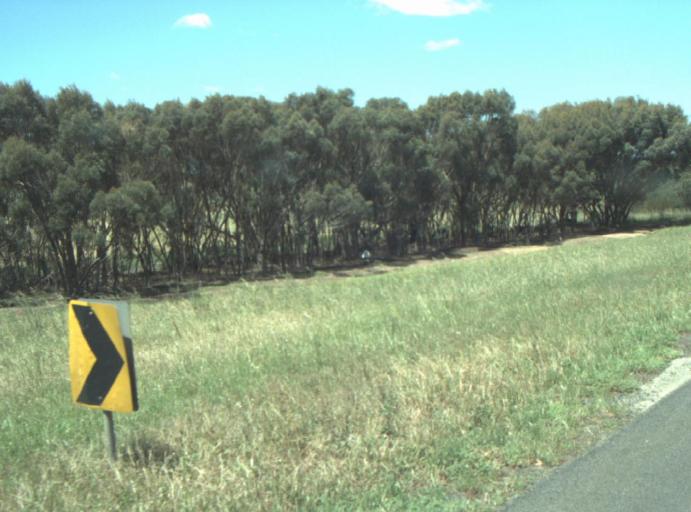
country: AU
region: Victoria
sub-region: Greater Geelong
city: Lara
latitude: -37.9033
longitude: 144.3710
